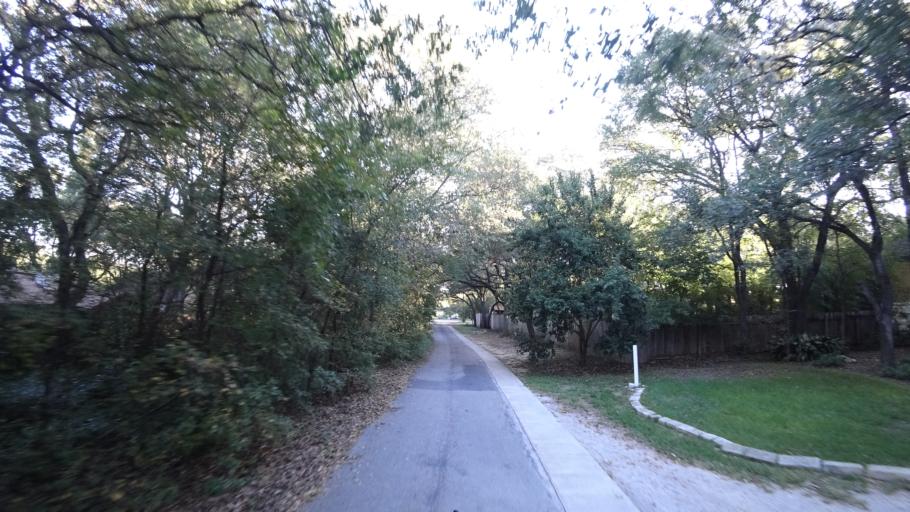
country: US
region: Texas
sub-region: Travis County
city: West Lake Hills
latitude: 30.3450
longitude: -97.8083
